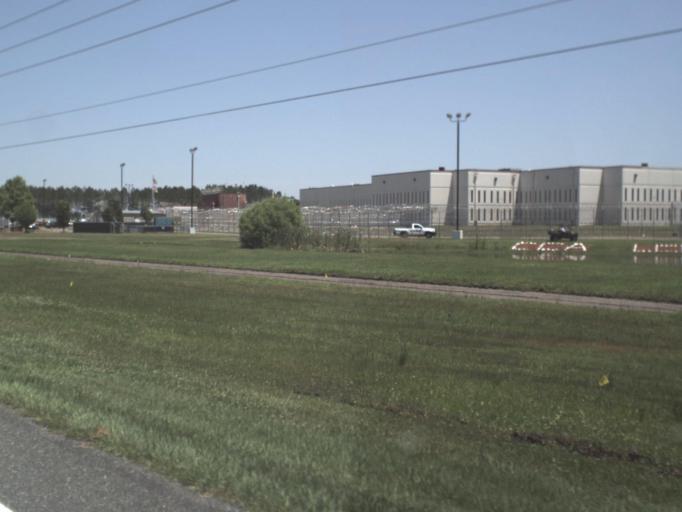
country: US
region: Florida
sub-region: Columbia County
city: Watertown
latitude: 30.1939
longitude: -82.5098
